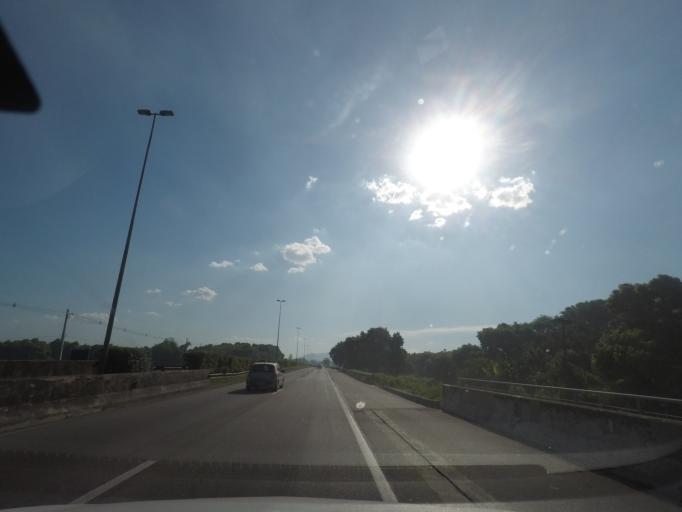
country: BR
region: Rio de Janeiro
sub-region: Duque De Caxias
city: Duque de Caxias
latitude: -22.6597
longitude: -43.2513
